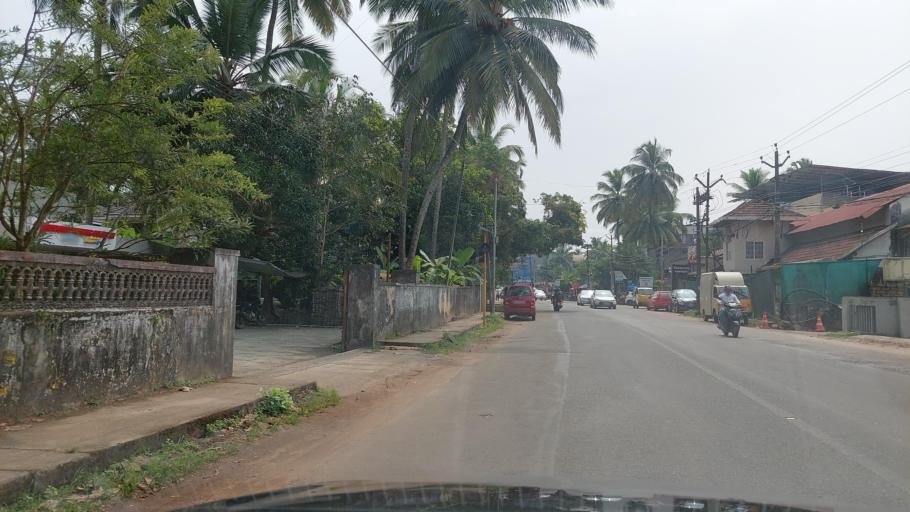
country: IN
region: Kerala
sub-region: Kozhikode
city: Kozhikode
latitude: 11.2936
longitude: 75.7644
